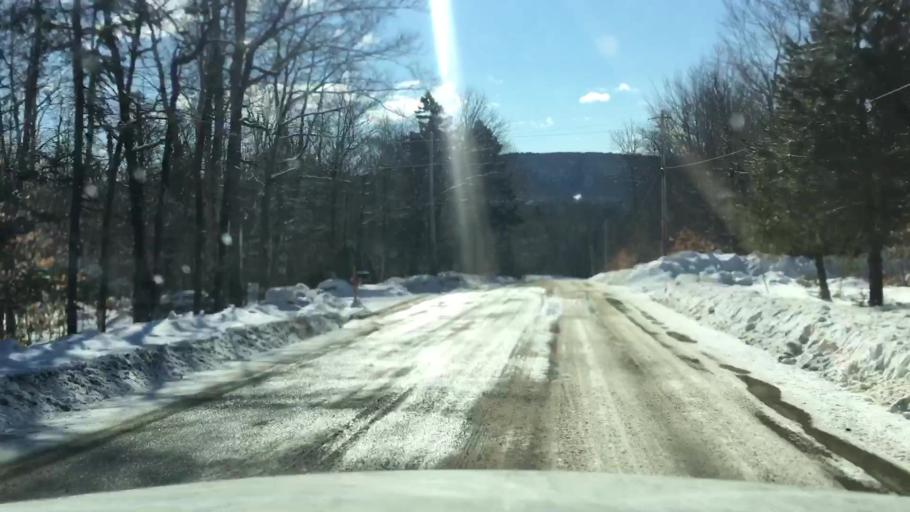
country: US
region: Maine
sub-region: Washington County
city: Calais
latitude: 45.0729
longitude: -67.5003
